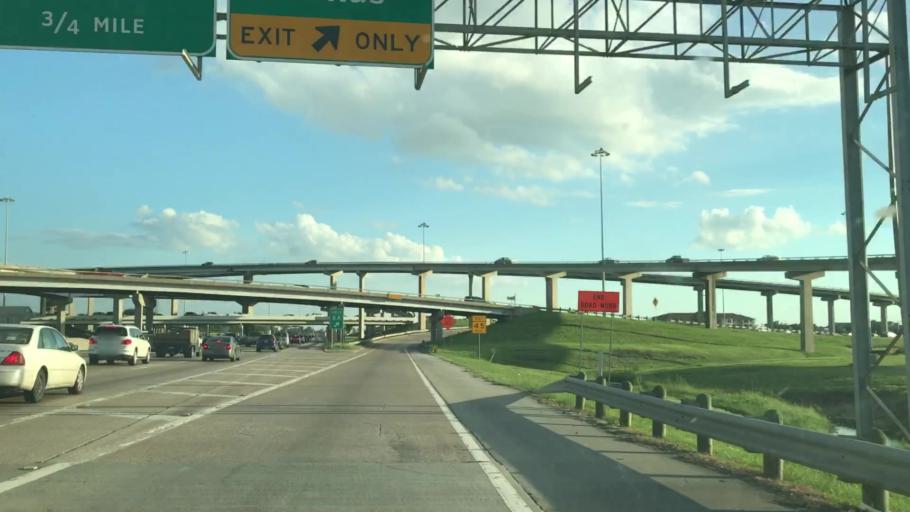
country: US
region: Texas
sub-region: Dallas County
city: Mesquite
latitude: 32.8254
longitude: -96.6305
